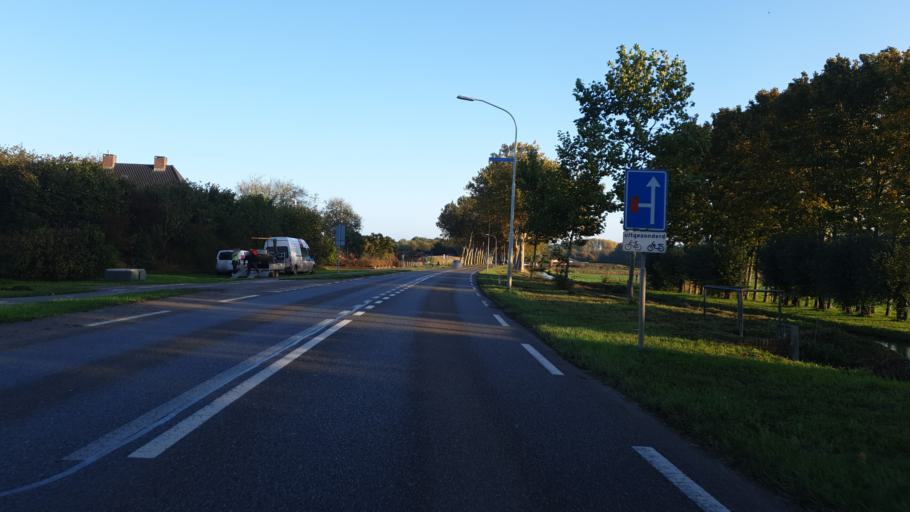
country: NL
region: Gelderland
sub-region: Gemeente Druten
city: Druten
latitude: 51.8753
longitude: 5.6096
